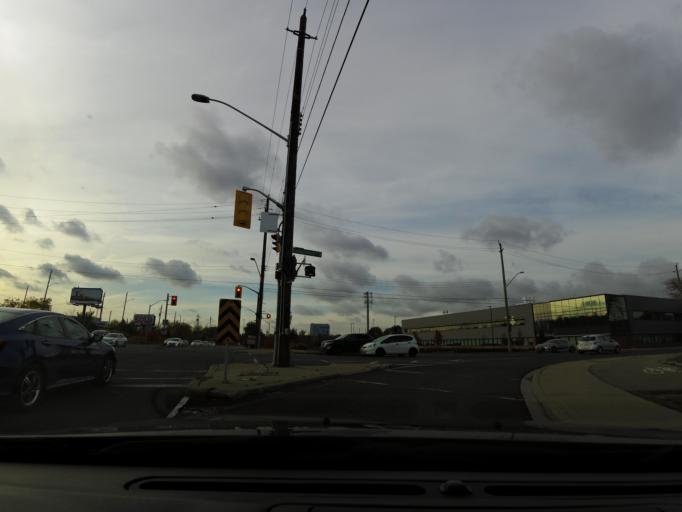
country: CA
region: Ontario
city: Hamilton
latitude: 43.2535
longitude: -79.9023
